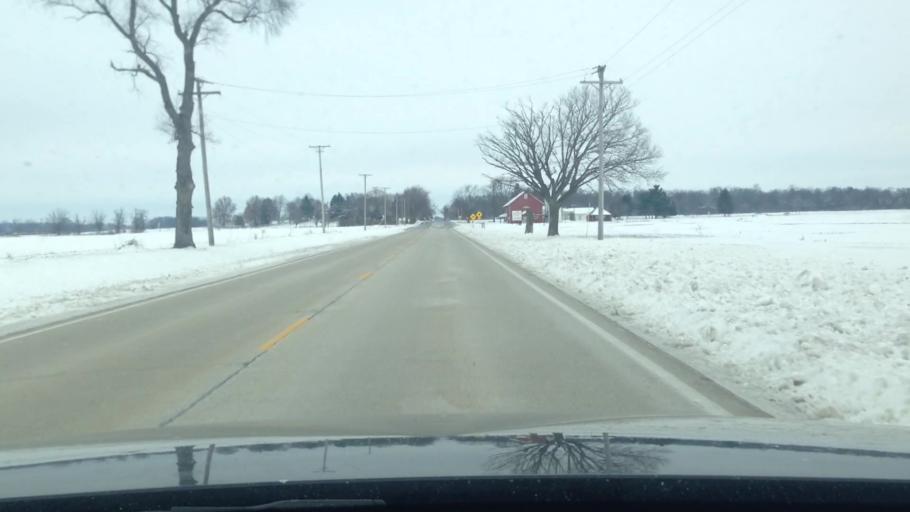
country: US
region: Illinois
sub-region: McHenry County
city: Hebron
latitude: 42.4108
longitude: -88.4381
